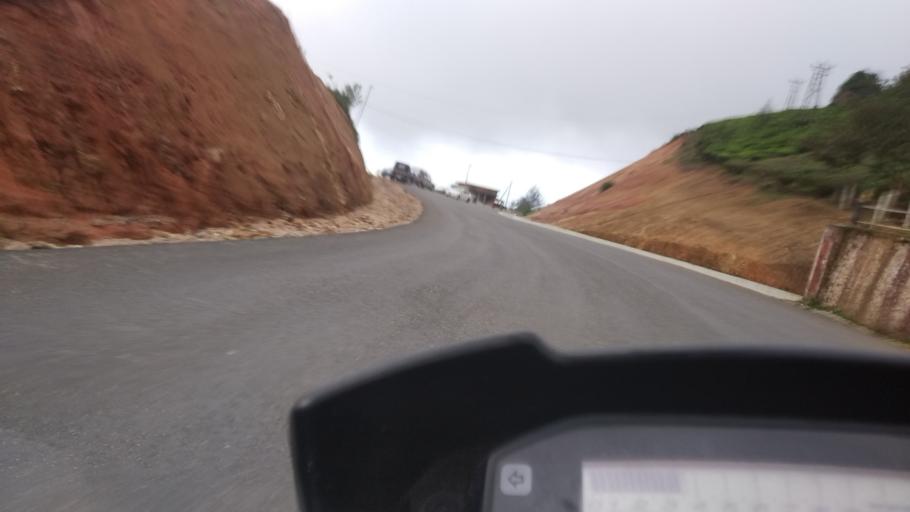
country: IN
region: Kerala
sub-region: Idukki
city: Munnar
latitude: 10.0351
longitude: 77.1580
